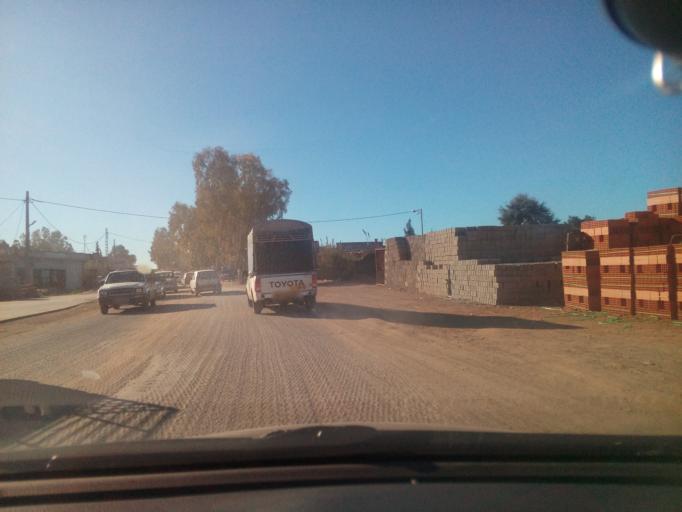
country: DZ
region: Mostaganem
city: Mostaganem
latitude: 35.8975
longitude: 0.2615
